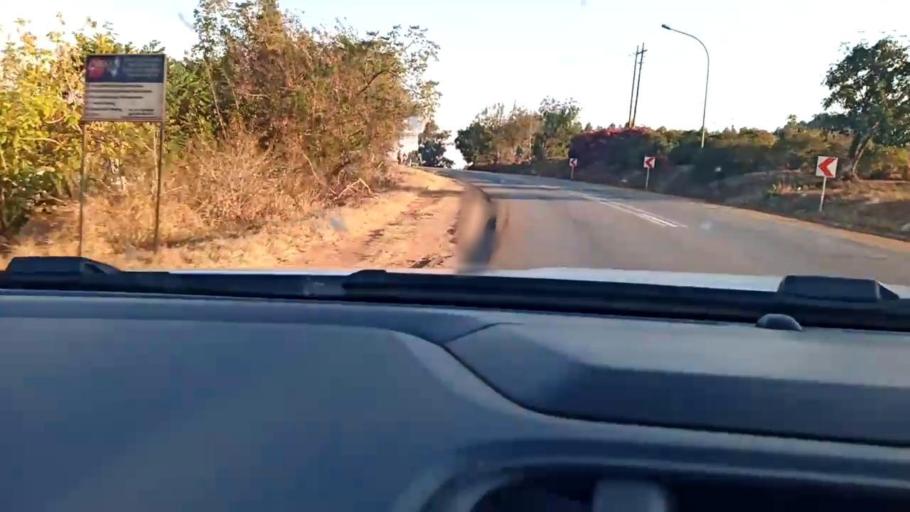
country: ZA
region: Limpopo
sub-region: Mopani District Municipality
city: Duiwelskloof
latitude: -23.6991
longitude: 30.1363
